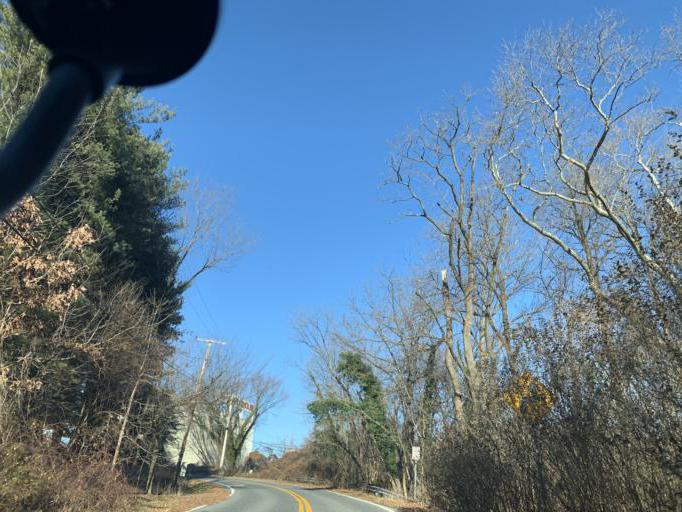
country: US
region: Maryland
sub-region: Baltimore County
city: Pikesville
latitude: 39.3847
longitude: -76.7364
